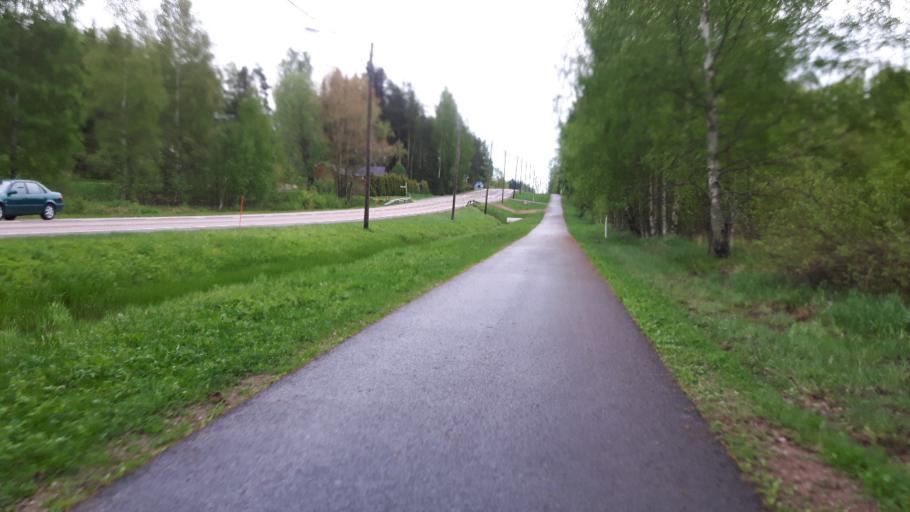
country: FI
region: Kymenlaakso
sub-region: Kotka-Hamina
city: Hamina
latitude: 60.5642
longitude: 27.1430
